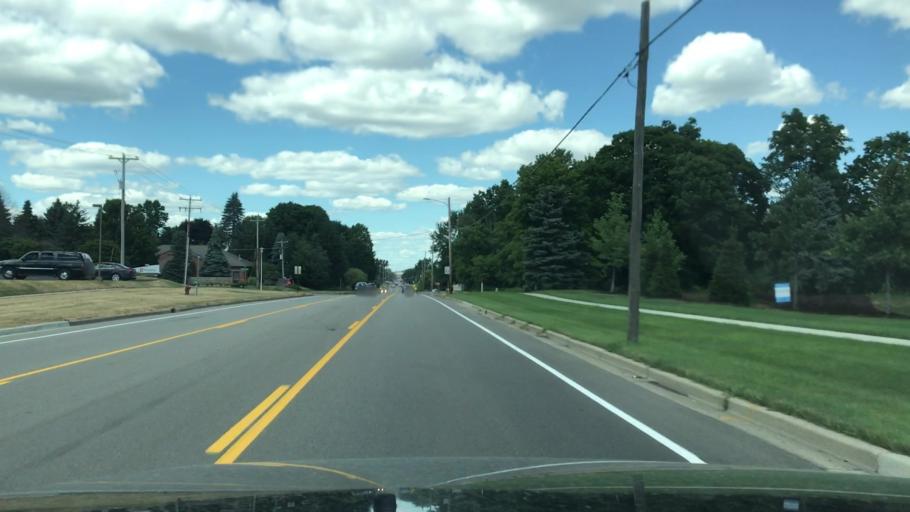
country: US
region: Michigan
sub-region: Kent County
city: Byron Center
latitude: 42.8212
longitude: -85.7230
